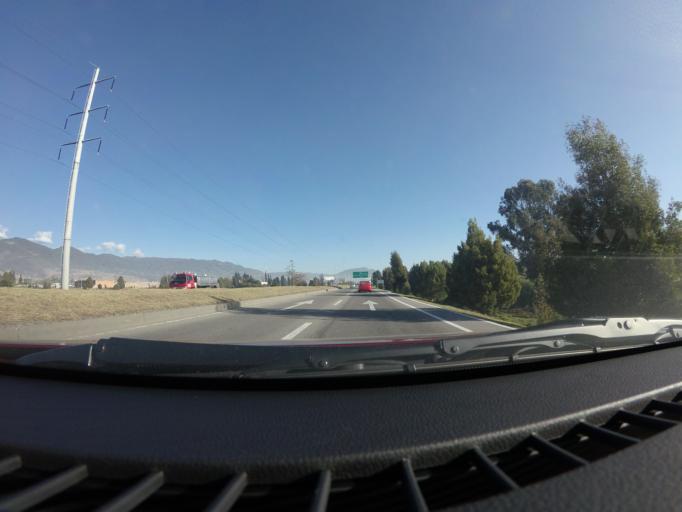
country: CO
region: Cundinamarca
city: Zipaquira
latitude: 5.0074
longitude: -73.9884
